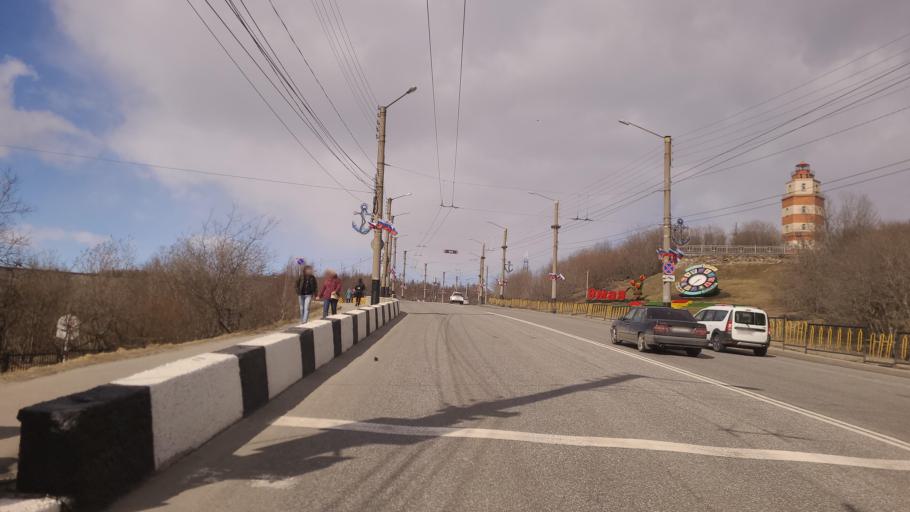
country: RU
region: Murmansk
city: Murmansk
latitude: 68.9839
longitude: 33.0932
